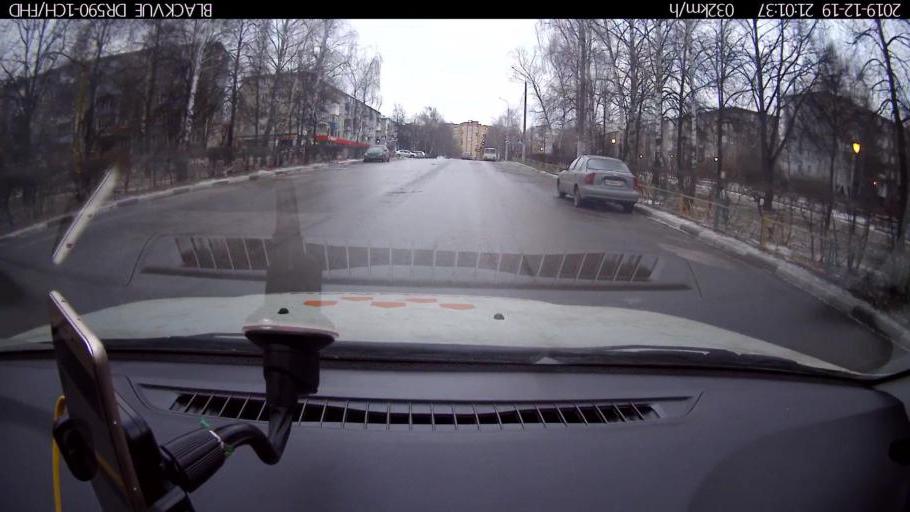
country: RU
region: Nizjnij Novgorod
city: Gorbatovka
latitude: 56.3463
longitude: 43.8530
